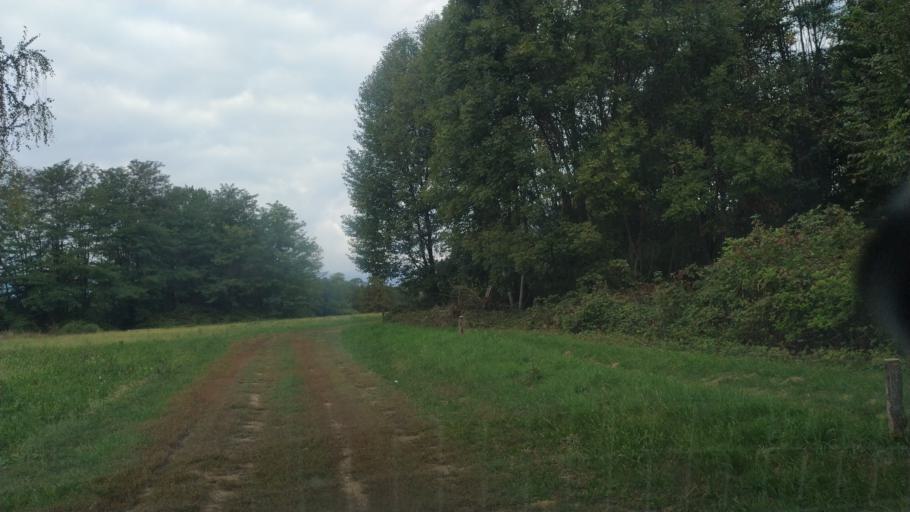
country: IT
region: Piedmont
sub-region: Provincia di Novara
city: Grignasco
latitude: 45.6768
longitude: 8.3350
